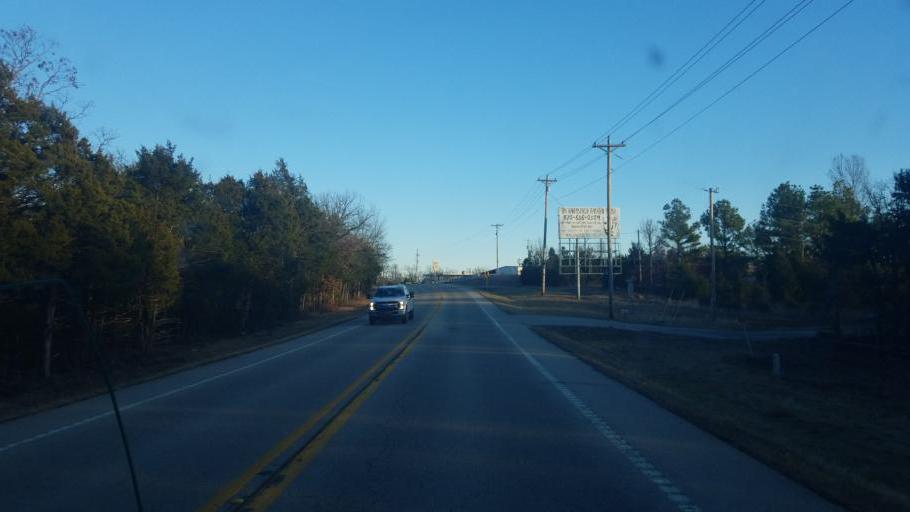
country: US
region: Arkansas
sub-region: Baxter County
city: Mountain Home
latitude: 36.3848
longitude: -92.1757
